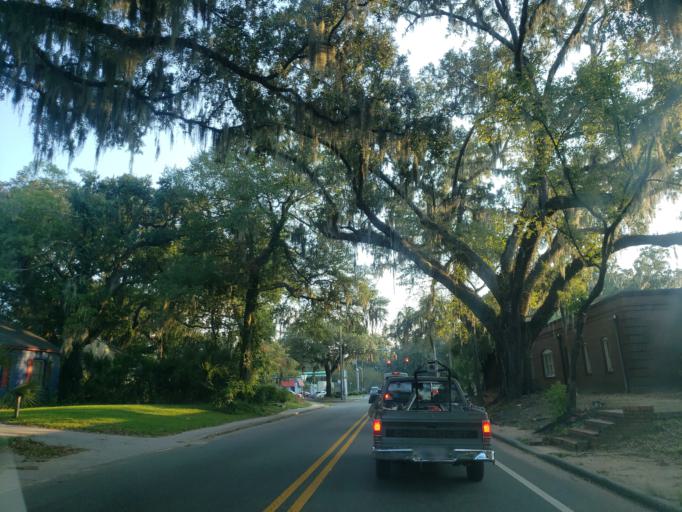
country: US
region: Georgia
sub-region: Chatham County
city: Thunderbolt
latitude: 32.0466
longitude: -81.0764
